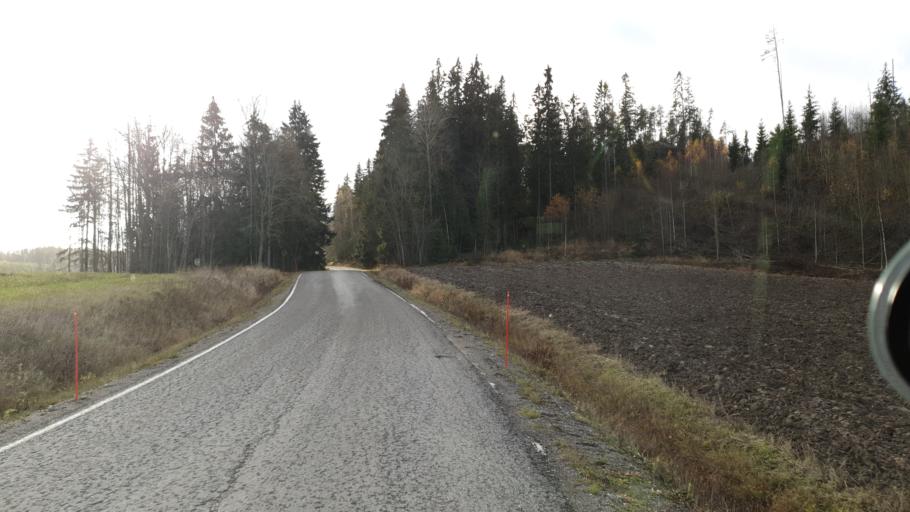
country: FI
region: Uusimaa
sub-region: Helsinki
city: Siuntio
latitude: 60.2522
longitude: 24.2986
